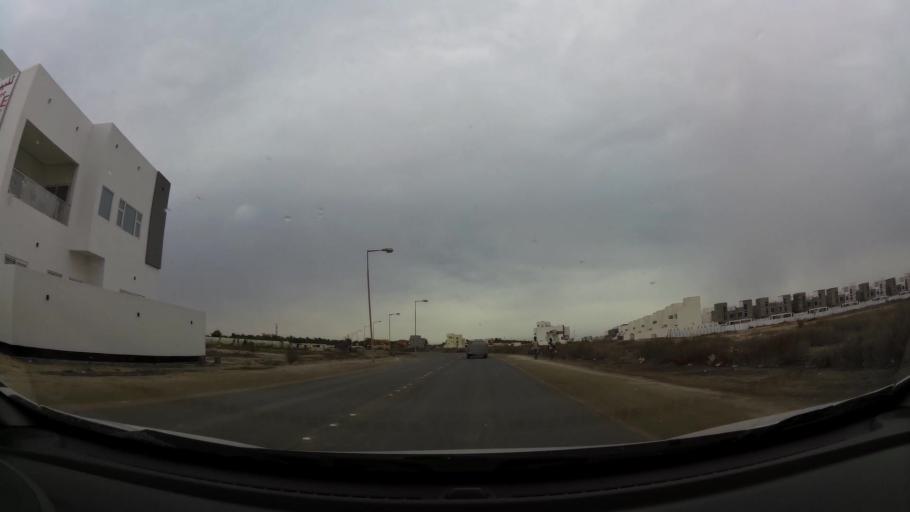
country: BH
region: Central Governorate
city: Madinat Hamad
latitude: 26.1327
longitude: 50.4681
